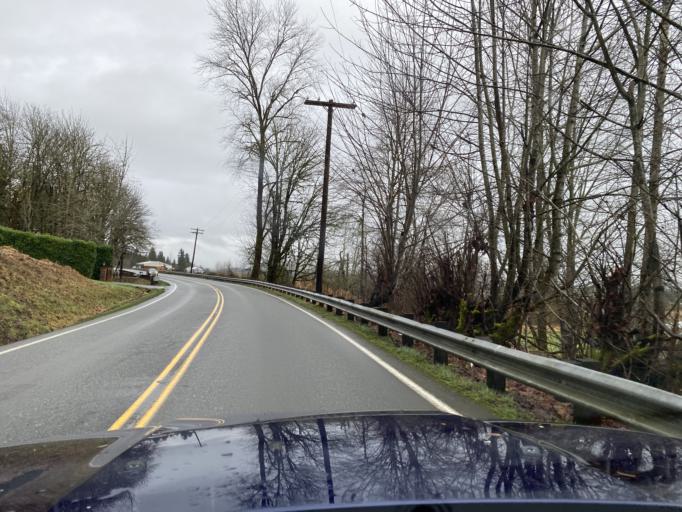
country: US
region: Washington
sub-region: King County
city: Duvall
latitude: 47.7484
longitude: -122.0045
